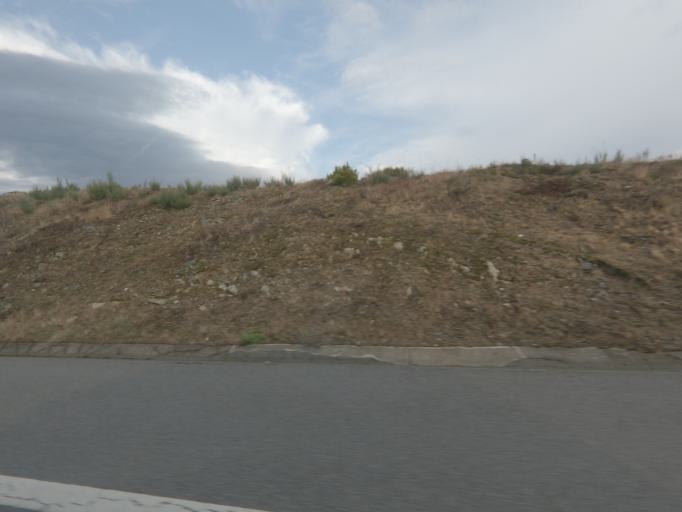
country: PT
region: Viseu
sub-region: Castro Daire
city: Castro Daire
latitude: 40.9764
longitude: -7.8855
